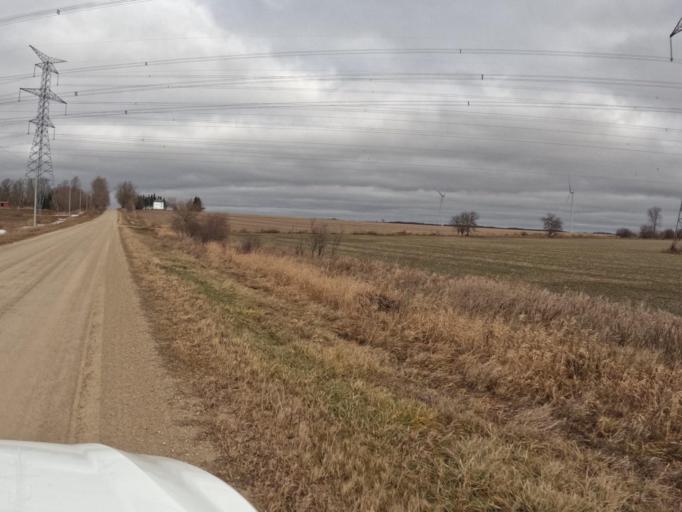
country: CA
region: Ontario
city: Shelburne
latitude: 43.9933
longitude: -80.4079
